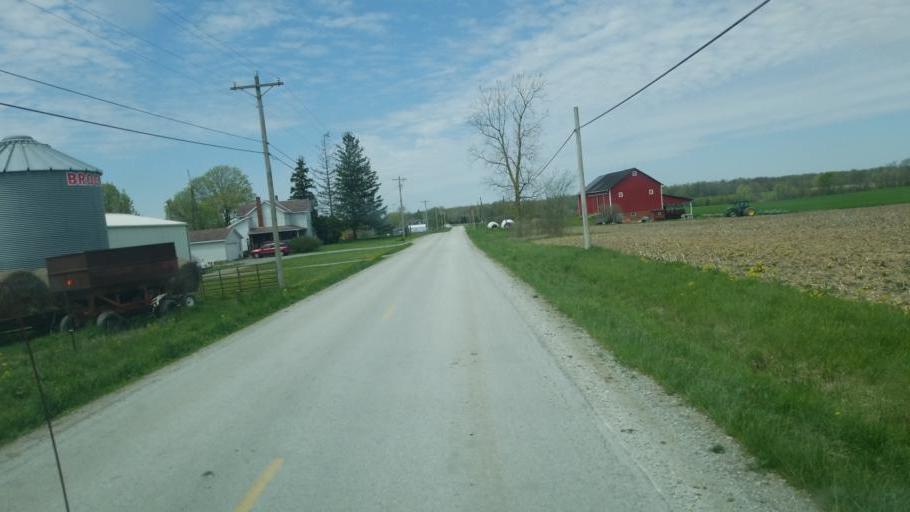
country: US
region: Ohio
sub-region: Hardin County
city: Ada
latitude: 40.7079
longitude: -83.7885
